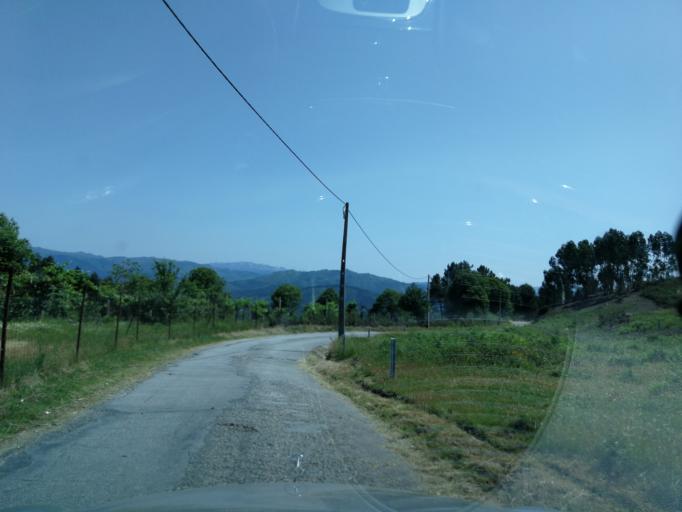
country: PT
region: Braga
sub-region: Povoa de Lanhoso
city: Povoa de Lanhoso
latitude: 41.5813
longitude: -8.3236
